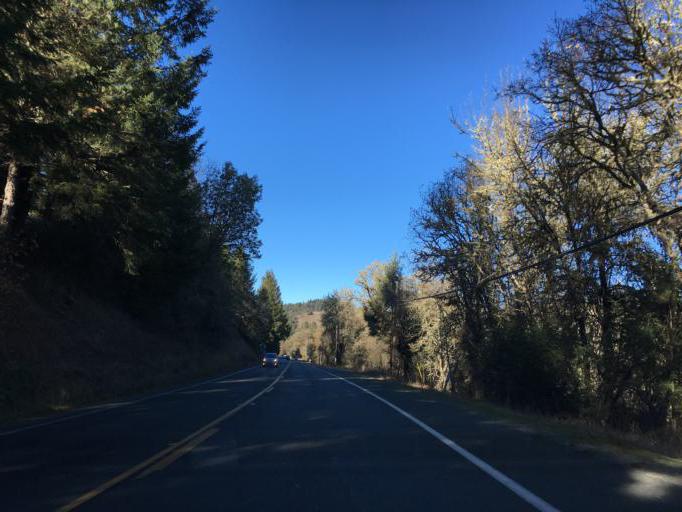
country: US
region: California
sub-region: Mendocino County
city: Brooktrails
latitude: 39.4510
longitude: -123.3480
